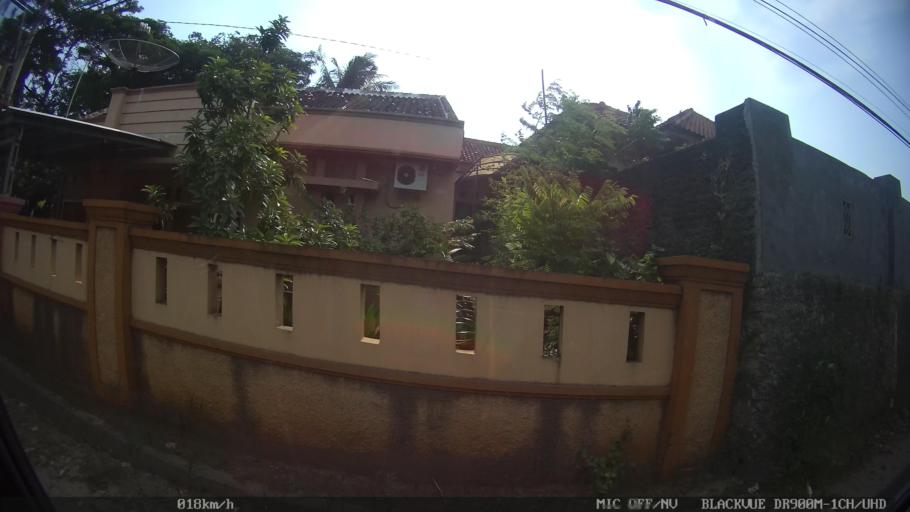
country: ID
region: Lampung
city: Kedaton
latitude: -5.3653
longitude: 105.2206
